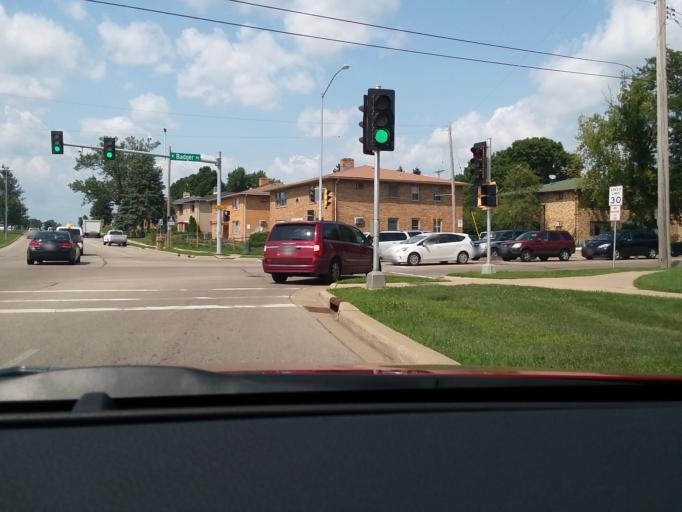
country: US
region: Wisconsin
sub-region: Dane County
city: Madison
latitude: 43.0384
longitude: -89.4039
